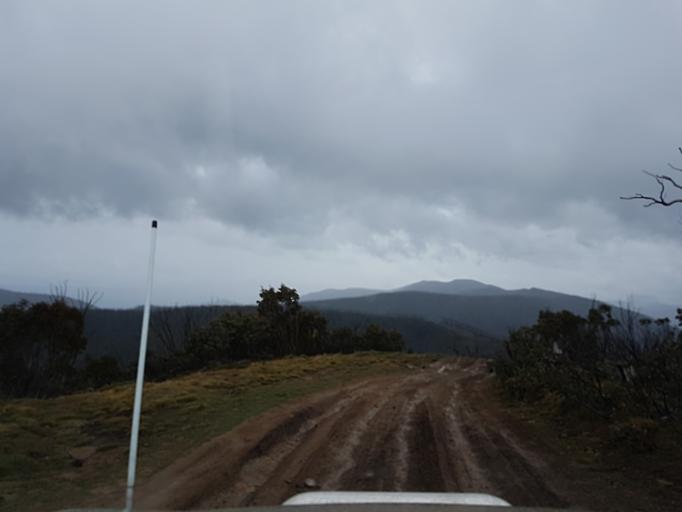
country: AU
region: Victoria
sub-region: Alpine
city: Mount Beauty
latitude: -37.0860
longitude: 147.1142
